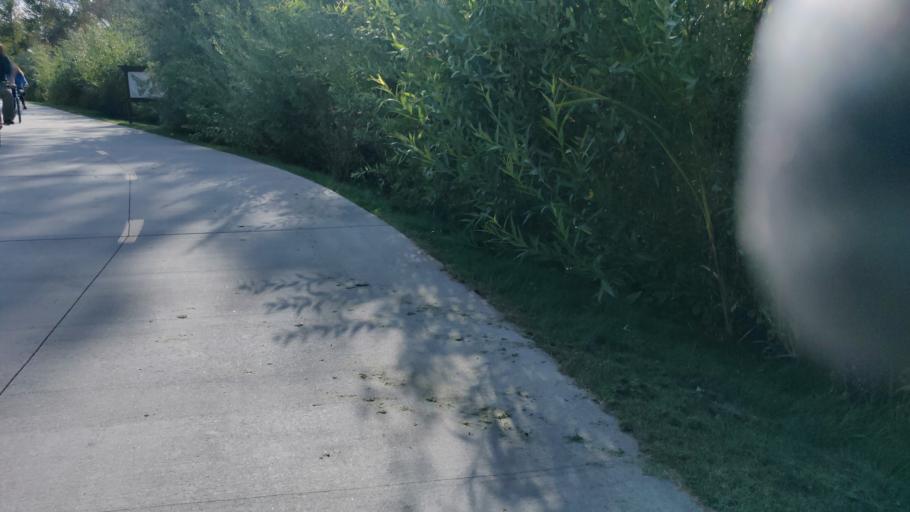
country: US
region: Idaho
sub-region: Ada County
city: Boise
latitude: 43.5779
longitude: -116.1508
